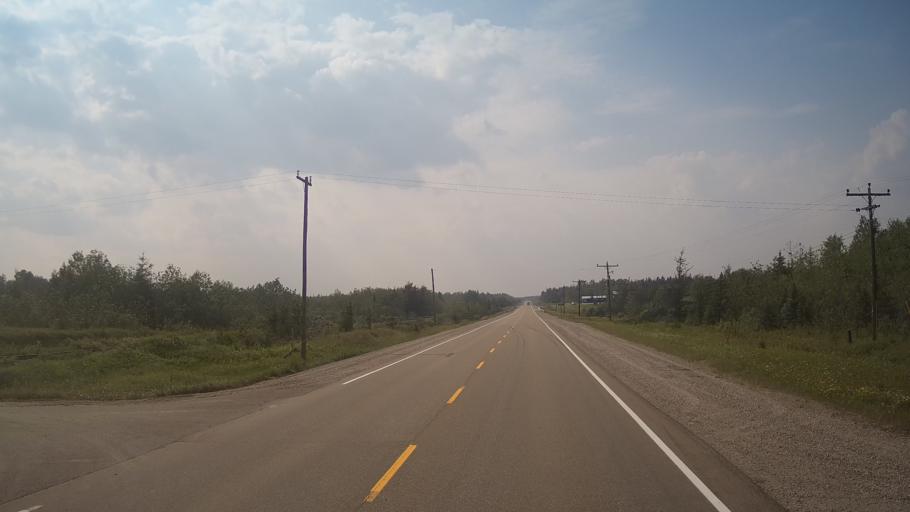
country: CA
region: Ontario
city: Kapuskasing
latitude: 49.4919
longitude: -82.7232
